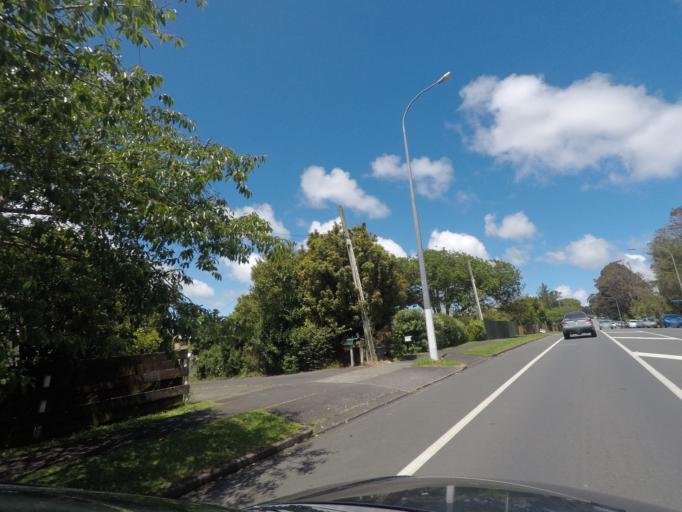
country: NZ
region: Auckland
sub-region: Auckland
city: Waitakere
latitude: -36.9031
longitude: 174.6546
